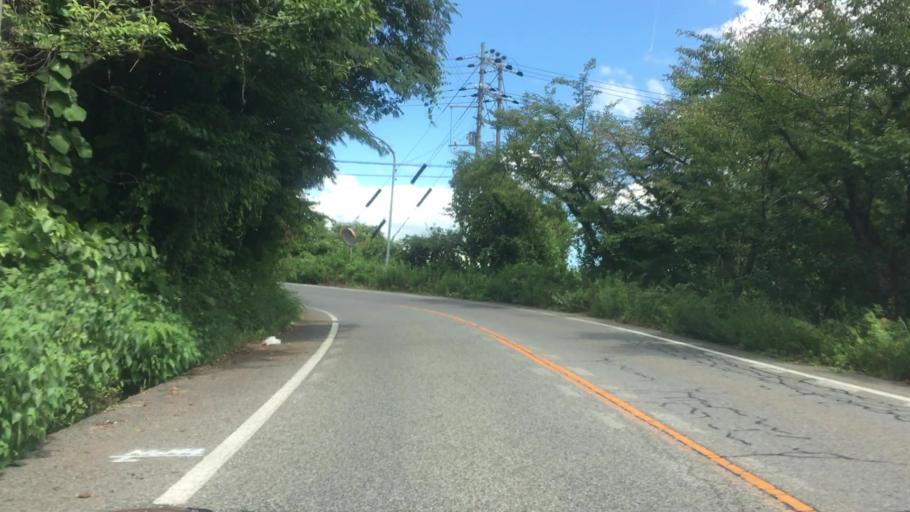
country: JP
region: Hyogo
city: Toyooka
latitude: 35.4908
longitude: 134.6891
